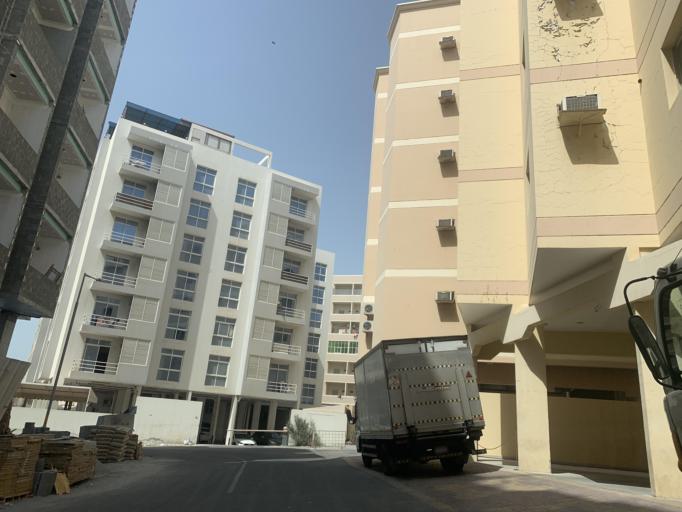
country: BH
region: Northern
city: Ar Rifa'
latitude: 26.1535
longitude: 50.5667
